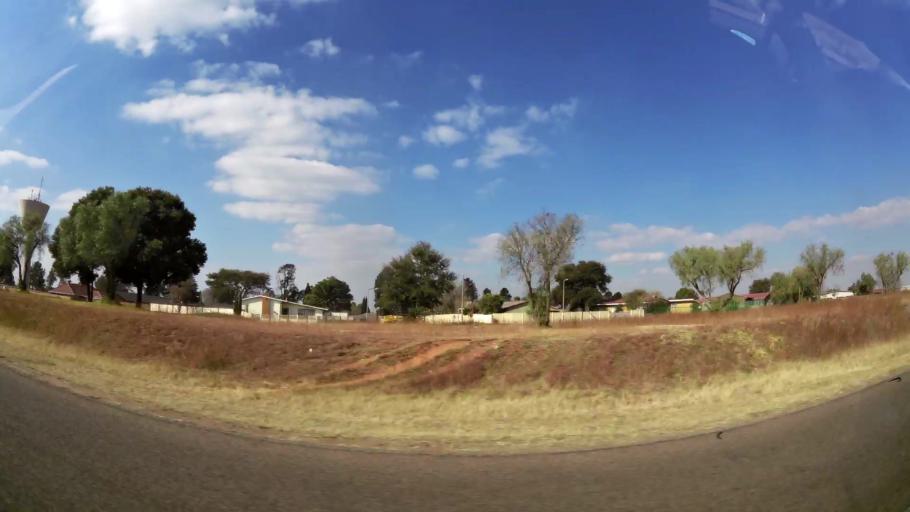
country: ZA
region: Gauteng
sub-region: West Rand District Municipality
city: Krugersdorp
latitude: -26.0733
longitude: 27.7613
